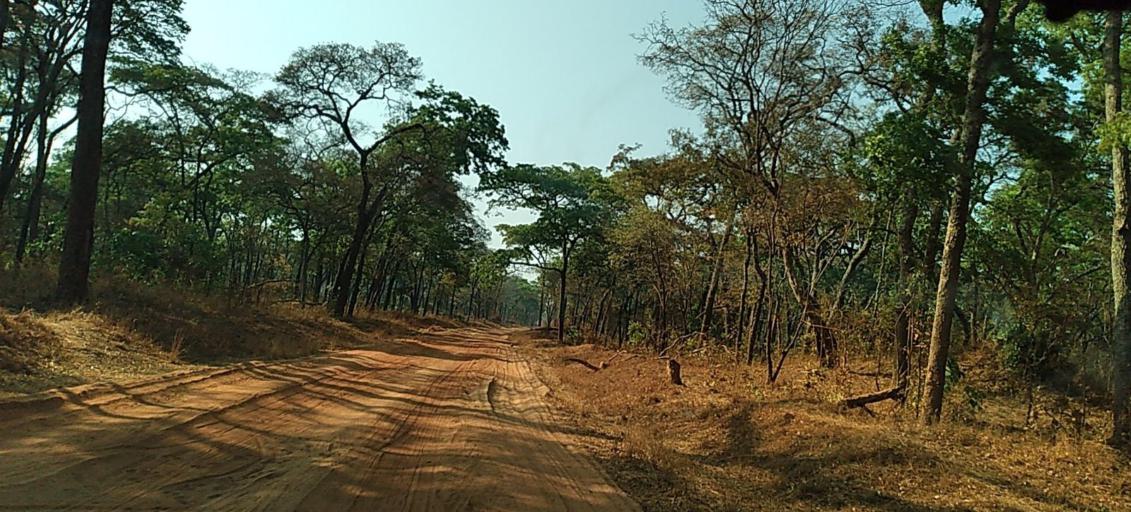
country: ZM
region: North-Western
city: Kasempa
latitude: -13.6287
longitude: 25.9867
